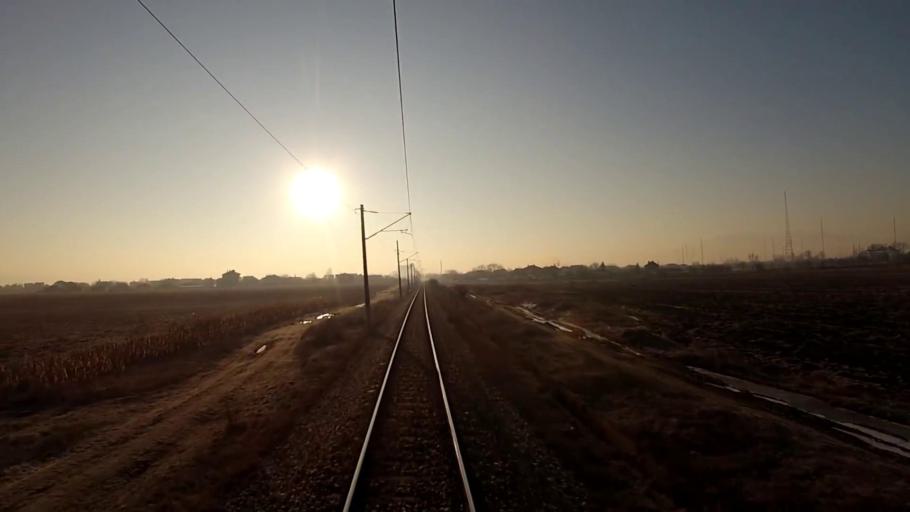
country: BG
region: Sofiya
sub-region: Obshtina Kostinbrod
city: Kostinbrod
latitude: 42.8068
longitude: 23.1998
